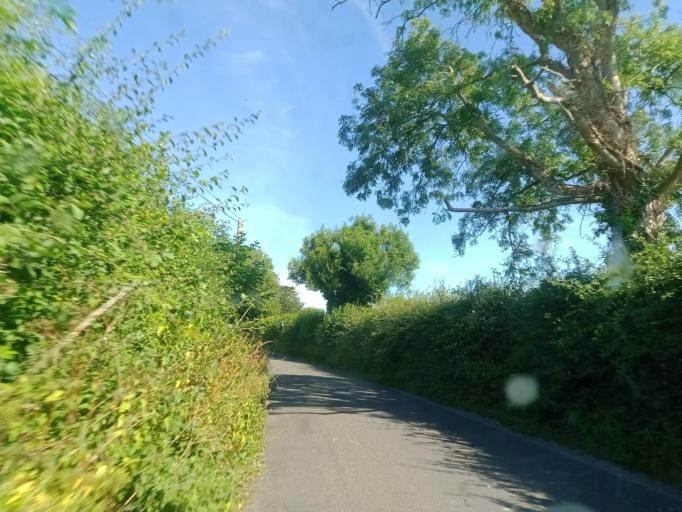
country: IE
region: Leinster
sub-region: Kilkenny
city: Ballyragget
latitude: 52.7556
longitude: -7.4025
